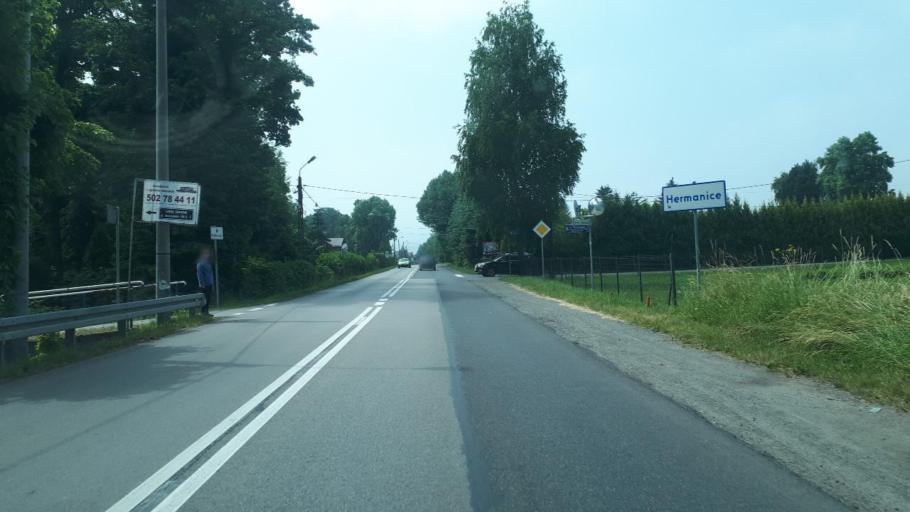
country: PL
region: Silesian Voivodeship
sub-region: Powiat cieszynski
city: Ustron
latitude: 49.7513
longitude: 18.8052
